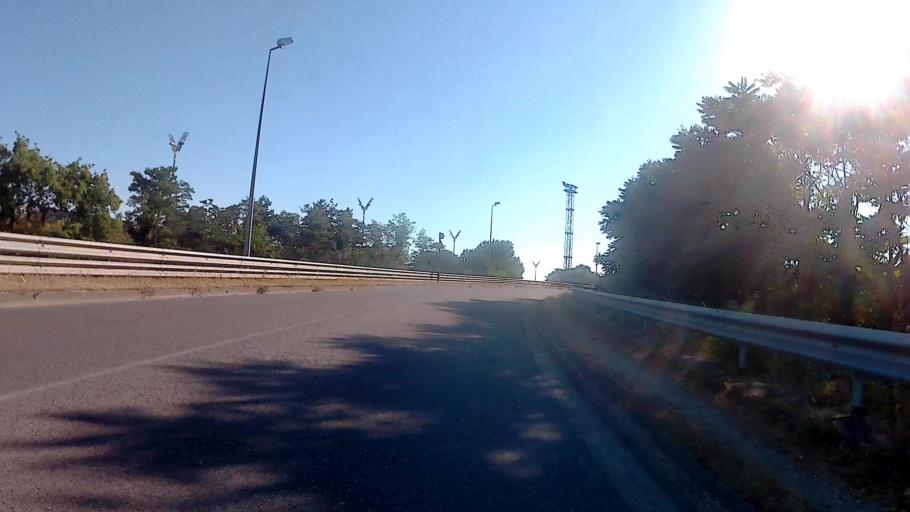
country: FR
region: Aquitaine
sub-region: Departement de la Gironde
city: Villenave-d'Ornon
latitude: 44.7805
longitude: -0.5482
